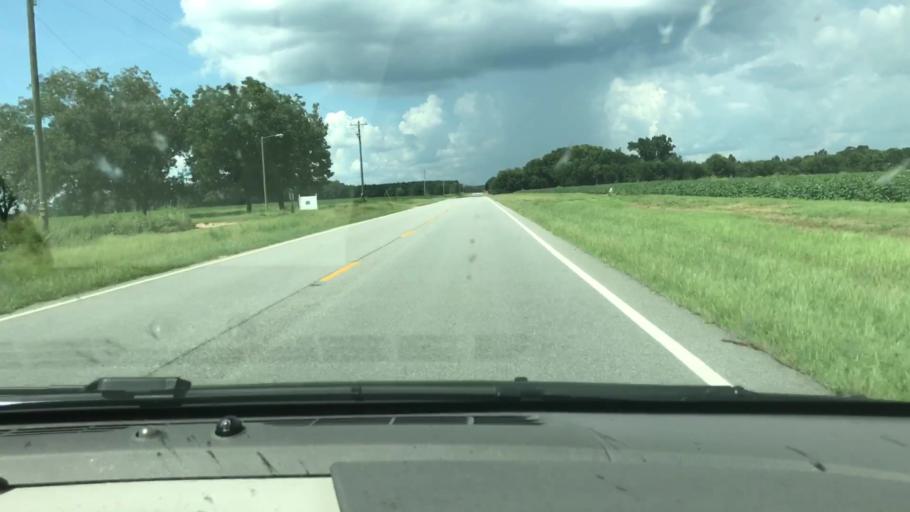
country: US
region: Georgia
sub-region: Quitman County
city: Georgetown
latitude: 31.8050
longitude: -85.0930
